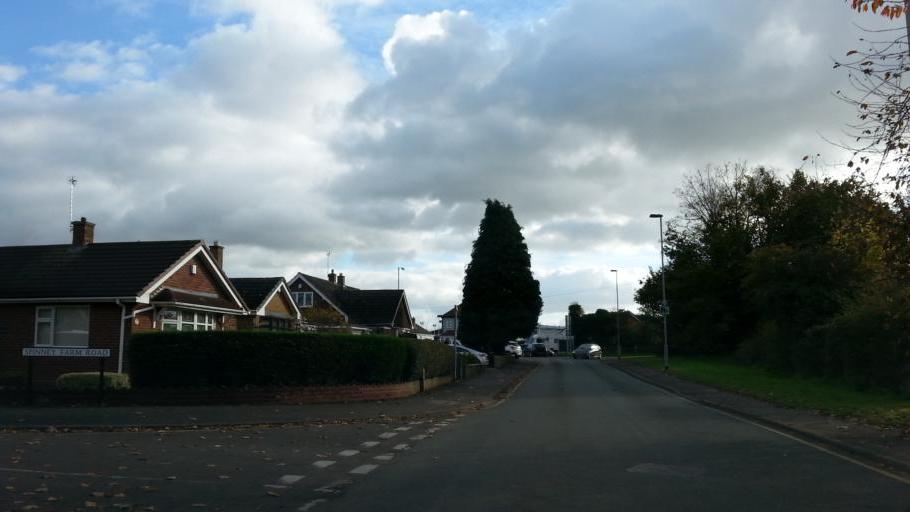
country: GB
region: England
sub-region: Staffordshire
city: Cannock
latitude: 52.6810
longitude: -2.0480
